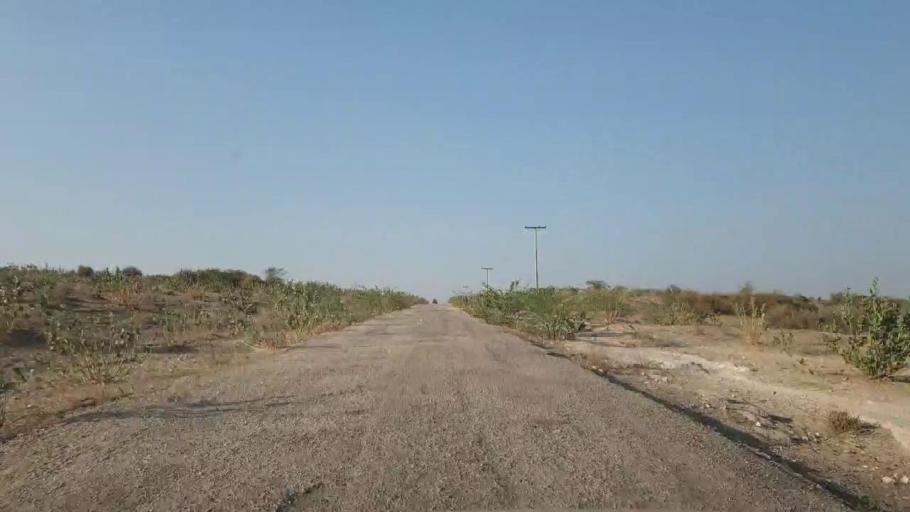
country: PK
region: Sindh
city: Chor
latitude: 25.6086
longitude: 69.8377
